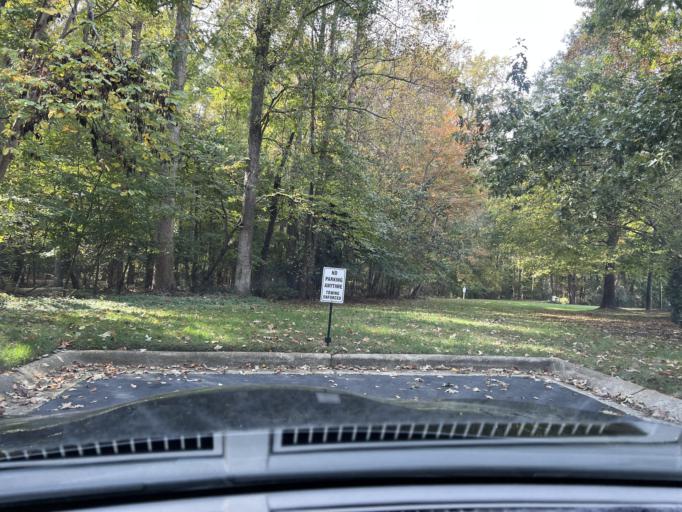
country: US
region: North Carolina
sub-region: Wake County
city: Wake Forest
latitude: 35.8946
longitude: -78.5847
